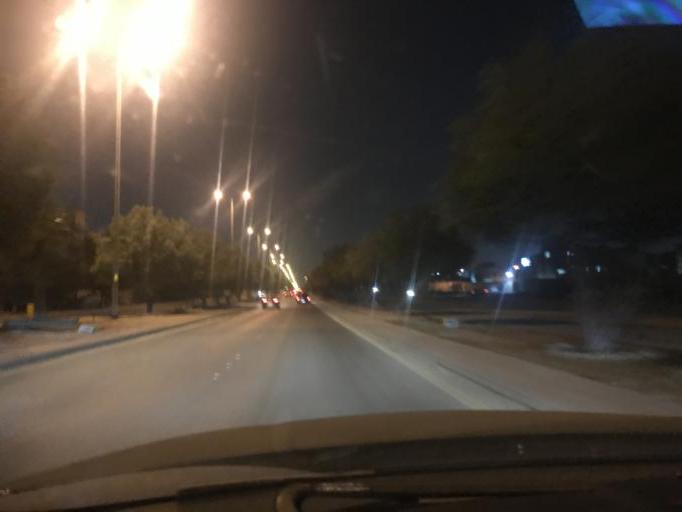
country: SA
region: Ar Riyad
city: Riyadh
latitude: 24.6810
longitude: 46.7940
